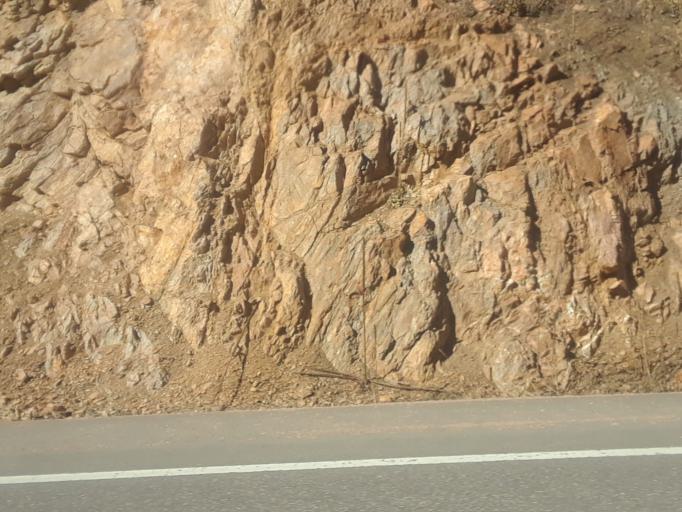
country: US
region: Colorado
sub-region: Boulder County
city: Boulder
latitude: 40.1058
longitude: -105.3273
